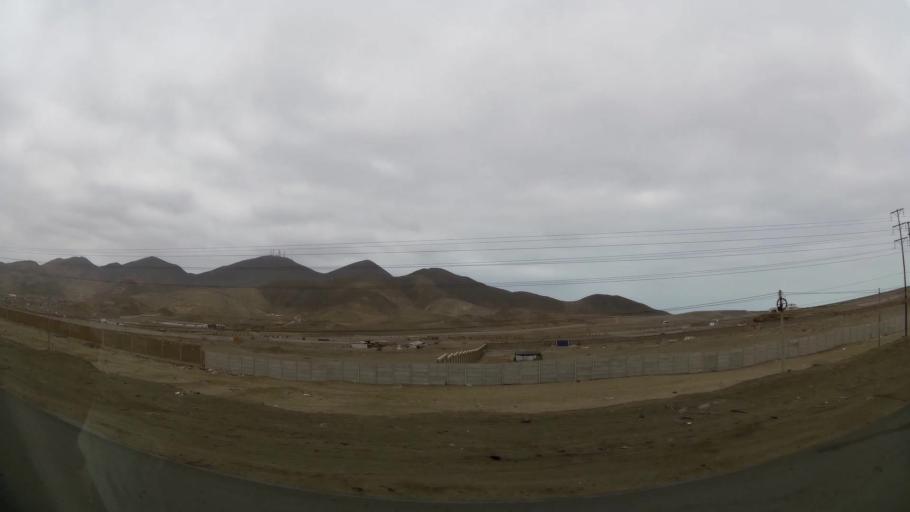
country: PE
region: Lima
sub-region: Lima
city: Pucusana
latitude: -12.4472
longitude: -76.7563
